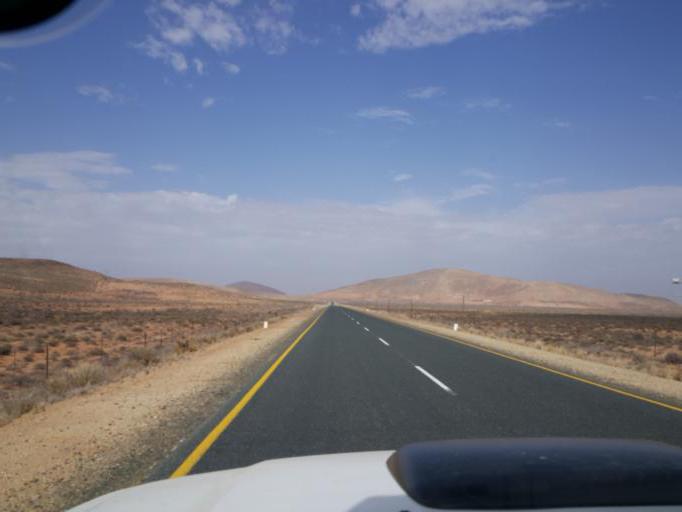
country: ZA
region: Northern Cape
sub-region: Namakwa District Municipality
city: Springbok
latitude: -29.2557
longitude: 17.5330
